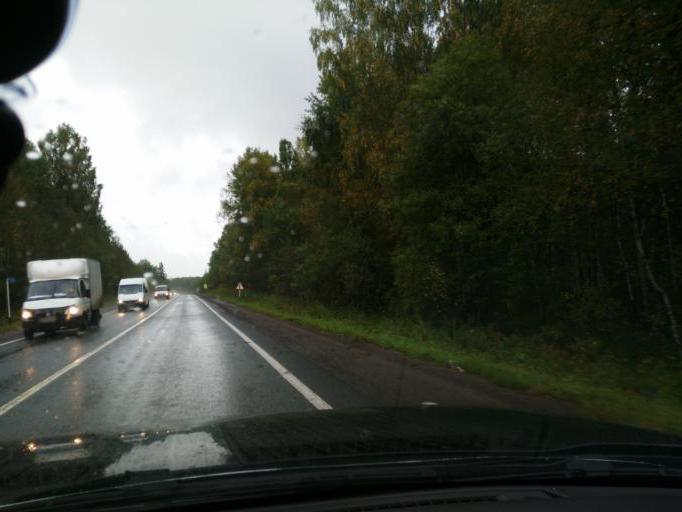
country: RU
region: Perm
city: Yugo-Kamskiy
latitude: 57.7368
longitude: 55.7091
